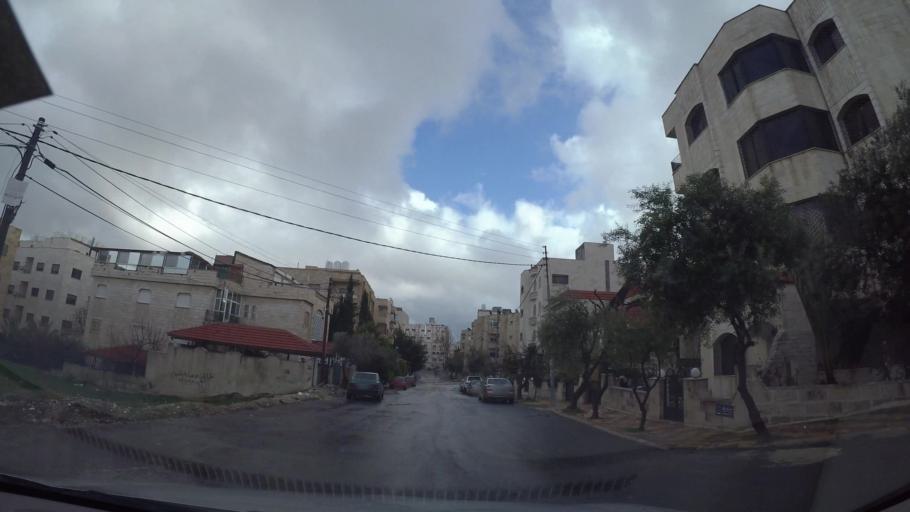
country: JO
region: Amman
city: Al Jubayhah
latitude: 32.0313
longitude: 35.8697
